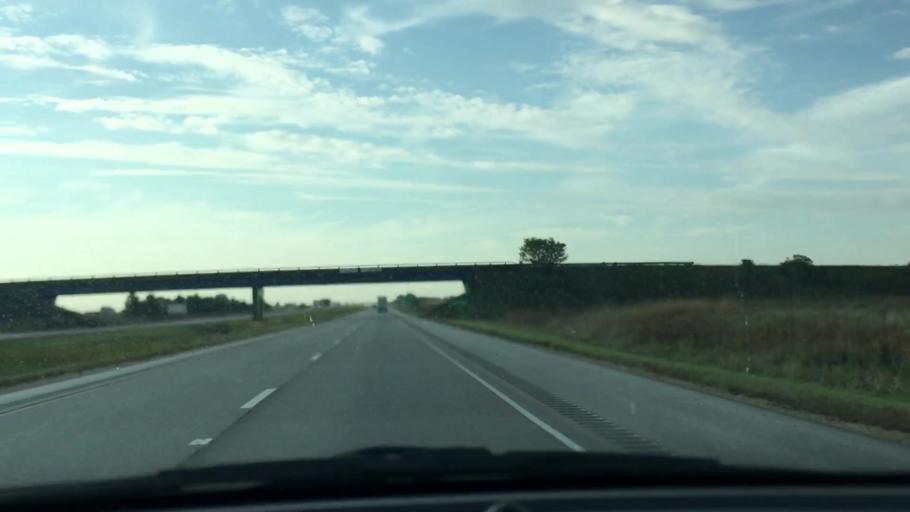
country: US
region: Illinois
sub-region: Ogle County
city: Hillcrest
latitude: 42.0228
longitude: -89.0212
